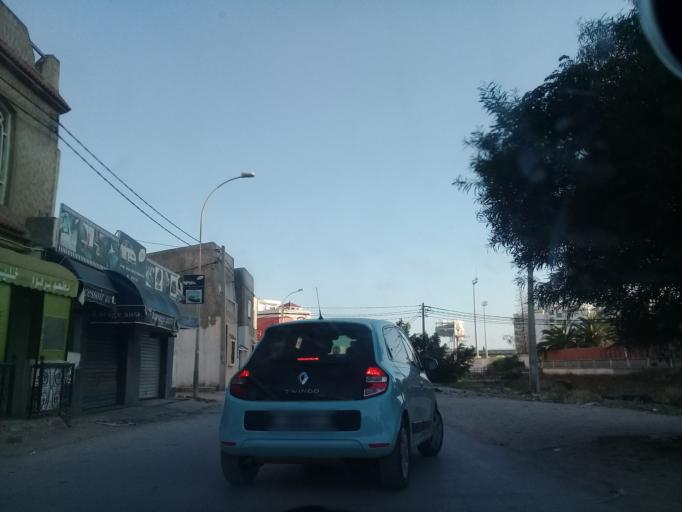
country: TN
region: Tunis
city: Tunis
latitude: 36.8318
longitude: 10.1899
